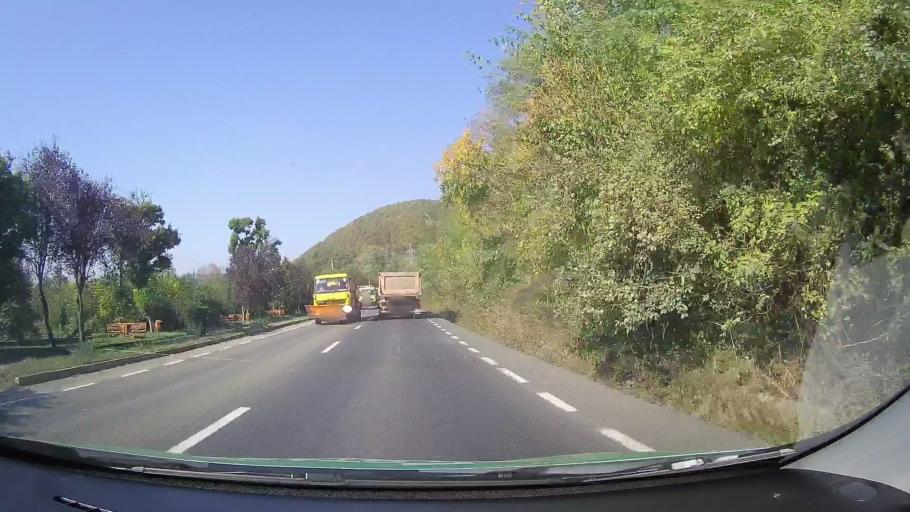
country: RO
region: Hunedoara
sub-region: Comuna Zam
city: Zam
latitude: 46.0107
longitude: 22.4392
